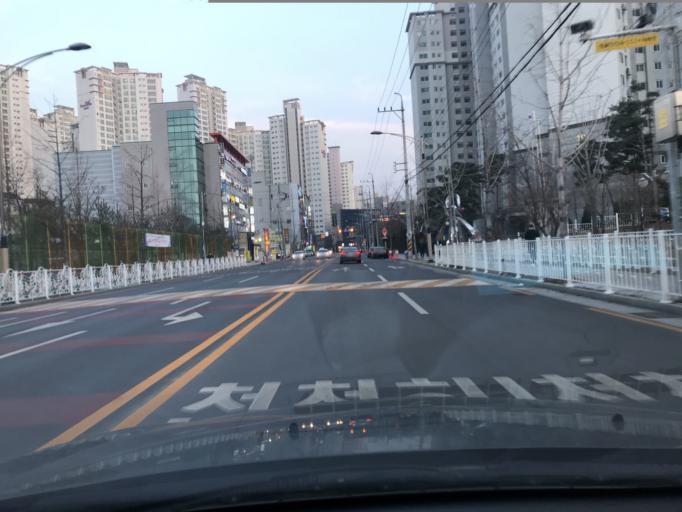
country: KR
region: Daegu
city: Hwawon
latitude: 35.8165
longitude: 128.5182
